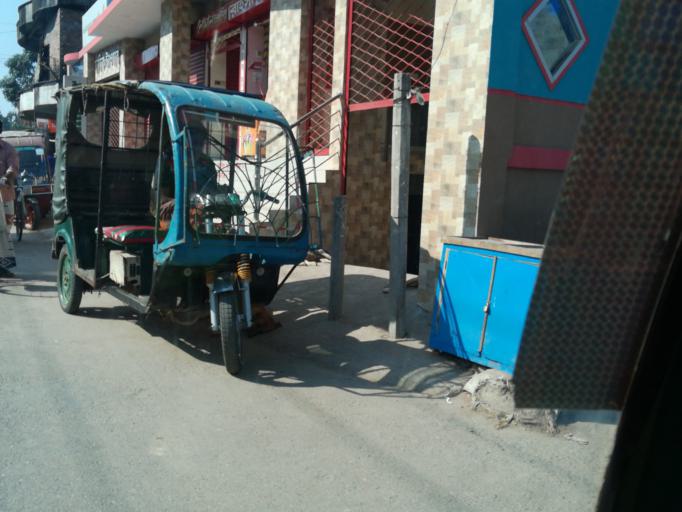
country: BD
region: Rangpur Division
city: Nageswari
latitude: 25.8139
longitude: 89.6500
